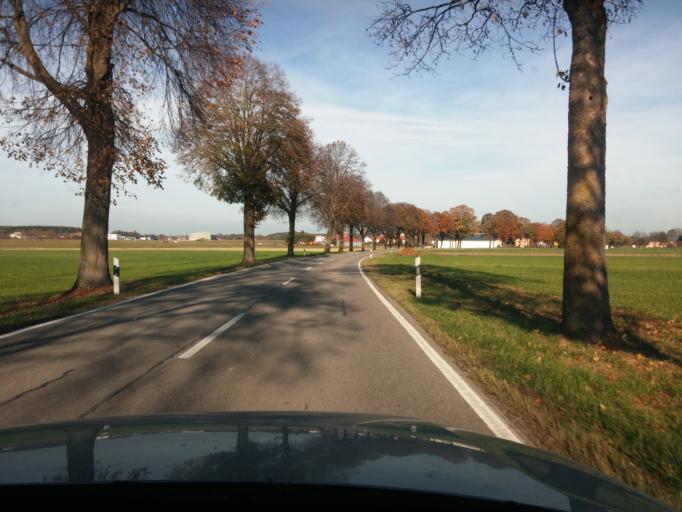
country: DE
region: Bavaria
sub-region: Upper Bavaria
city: Pastetten
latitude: 48.2032
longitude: 11.9525
